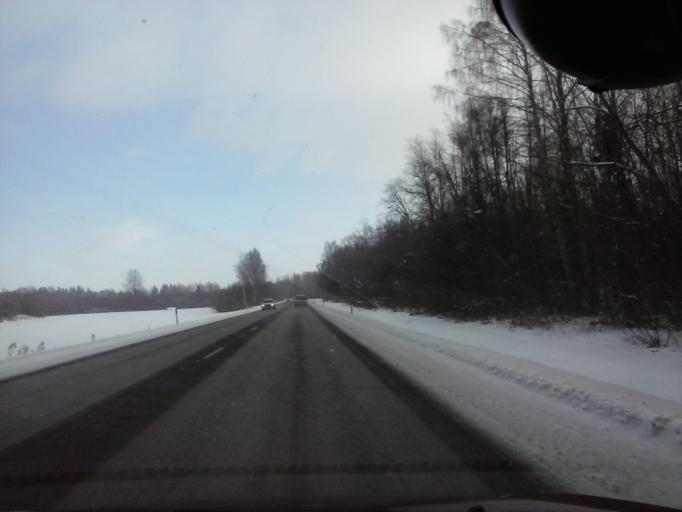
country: EE
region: Jogevamaa
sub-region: Poltsamaa linn
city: Poltsamaa
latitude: 58.3934
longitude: 25.9173
